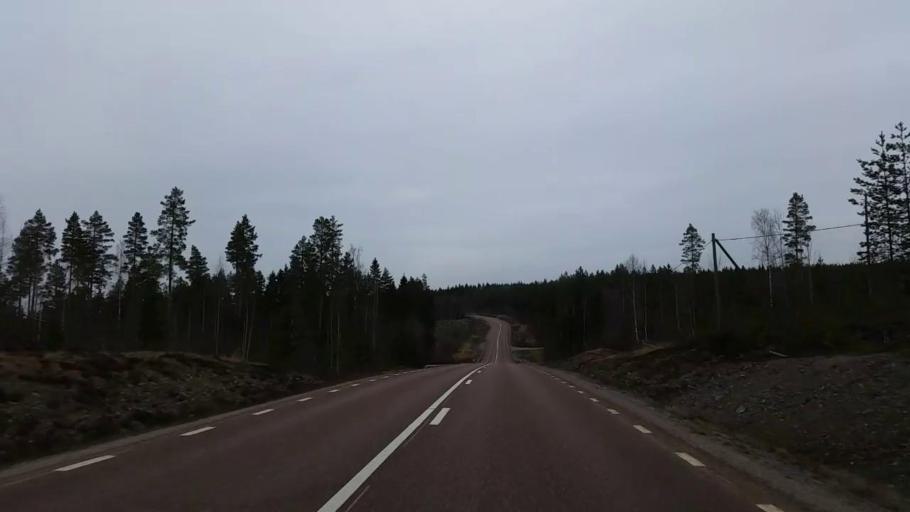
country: SE
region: Gaevleborg
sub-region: Ovanakers Kommun
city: Edsbyn
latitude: 61.2130
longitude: 15.8730
